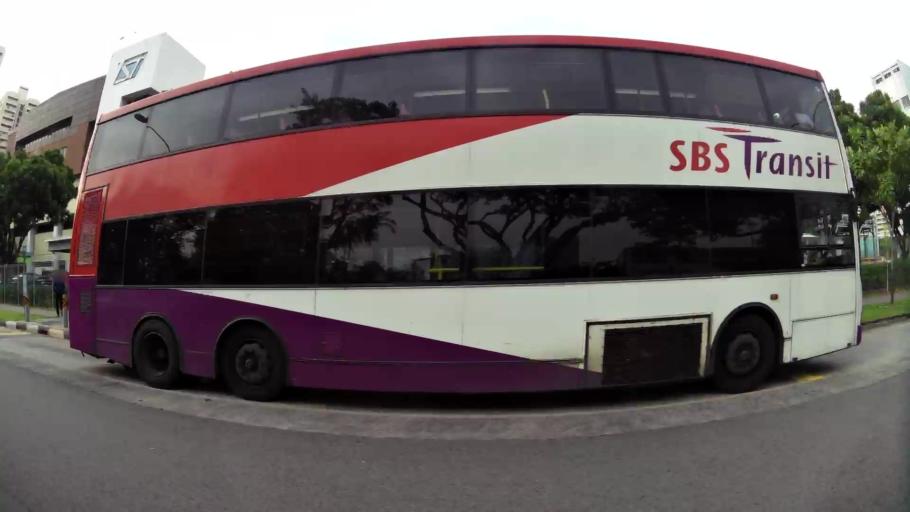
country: SG
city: Singapore
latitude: 1.3315
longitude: 103.8527
